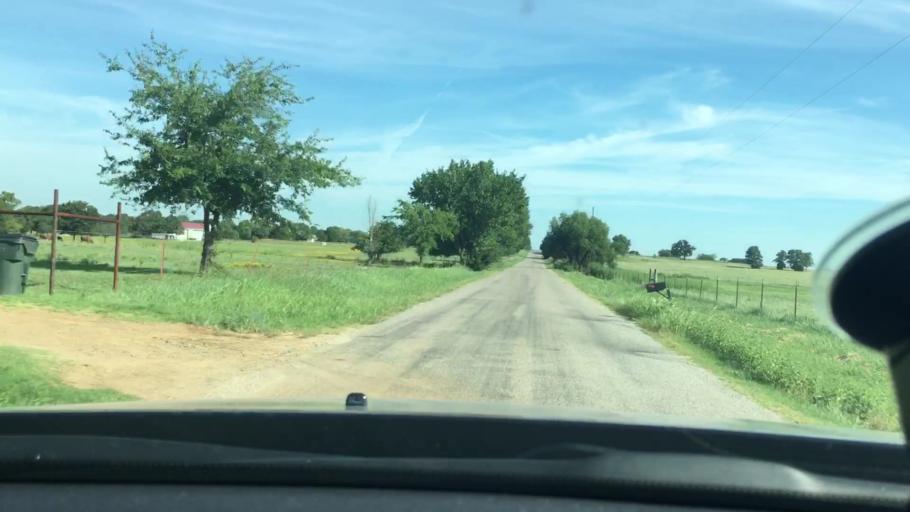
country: US
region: Oklahoma
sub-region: Carter County
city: Lone Grove
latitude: 34.2605
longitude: -97.2474
